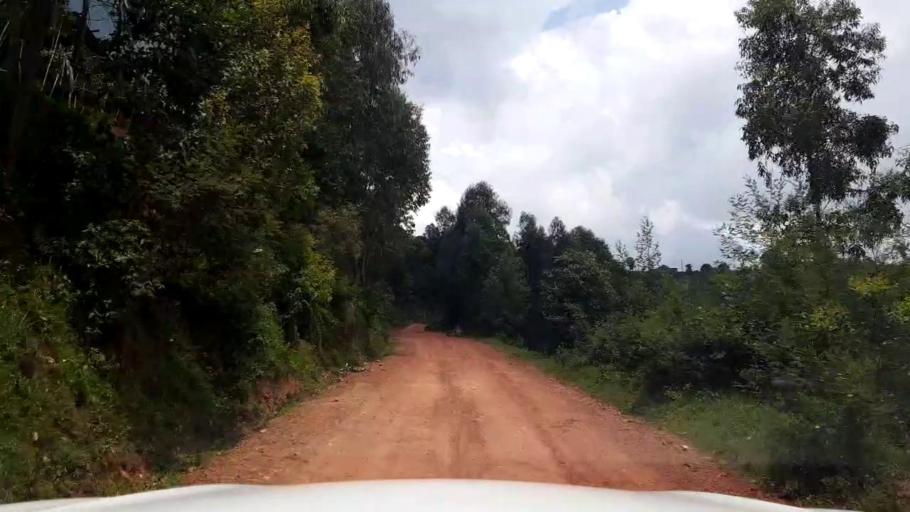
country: RW
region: Northern Province
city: Byumba
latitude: -1.4869
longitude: 29.9266
